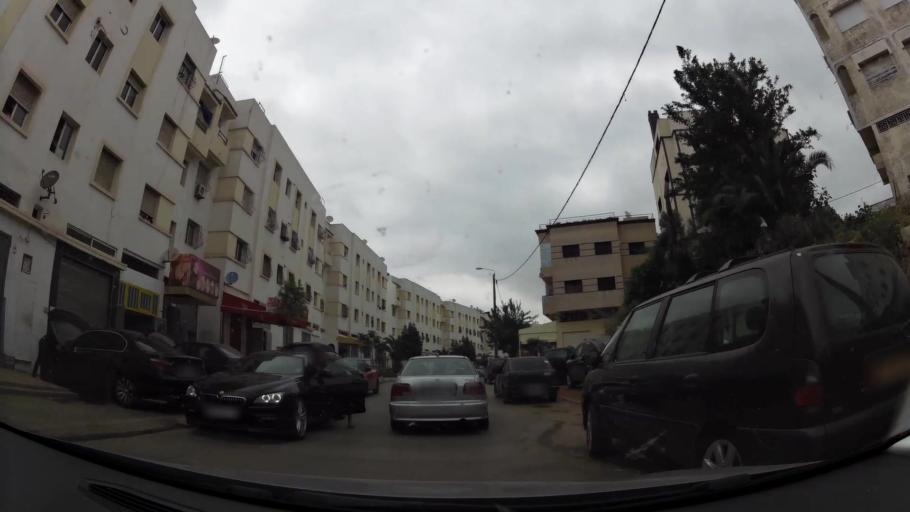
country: MA
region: Rabat-Sale-Zemmour-Zaer
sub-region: Rabat
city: Rabat
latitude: 33.9822
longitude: -6.8144
